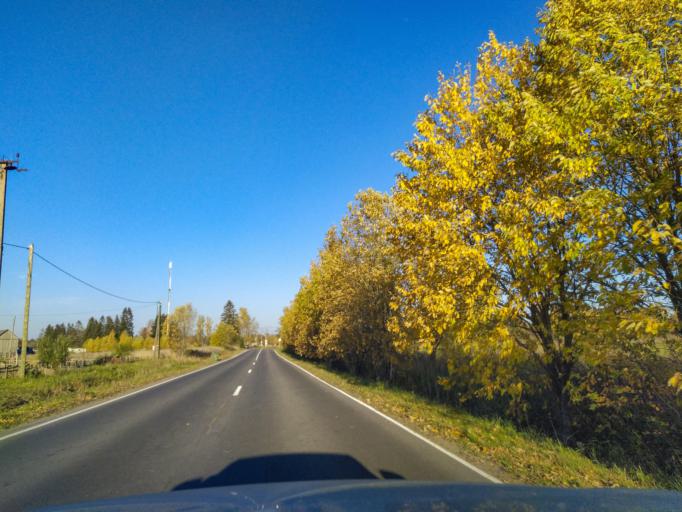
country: RU
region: Leningrad
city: Siverskiy
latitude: 59.3329
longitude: 30.0519
